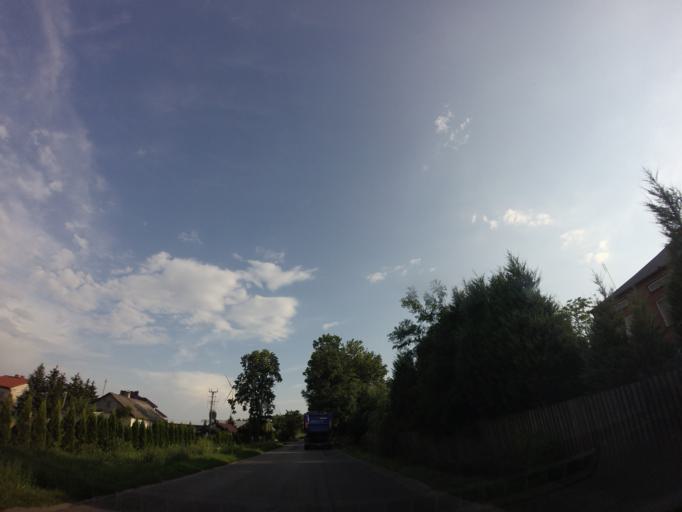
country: PL
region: Lublin Voivodeship
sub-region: Powiat lubartowski
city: Michow
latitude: 51.4930
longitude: 22.3043
